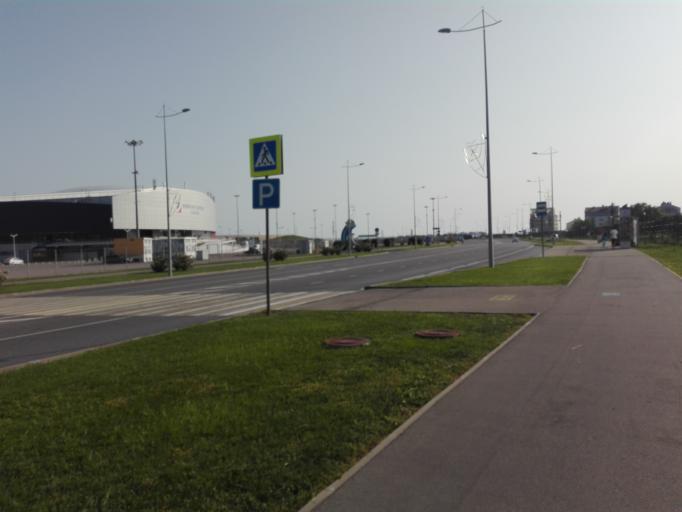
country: RU
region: Krasnodarskiy
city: Adler
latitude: 43.4086
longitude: 39.9489
